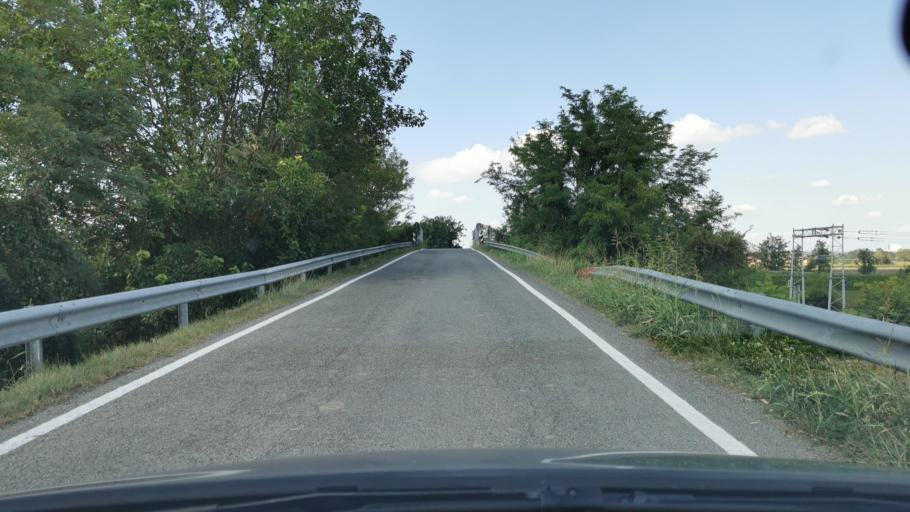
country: IT
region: Emilia-Romagna
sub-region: Provincia di Piacenza
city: Caorso
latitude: 45.0396
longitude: 9.8591
